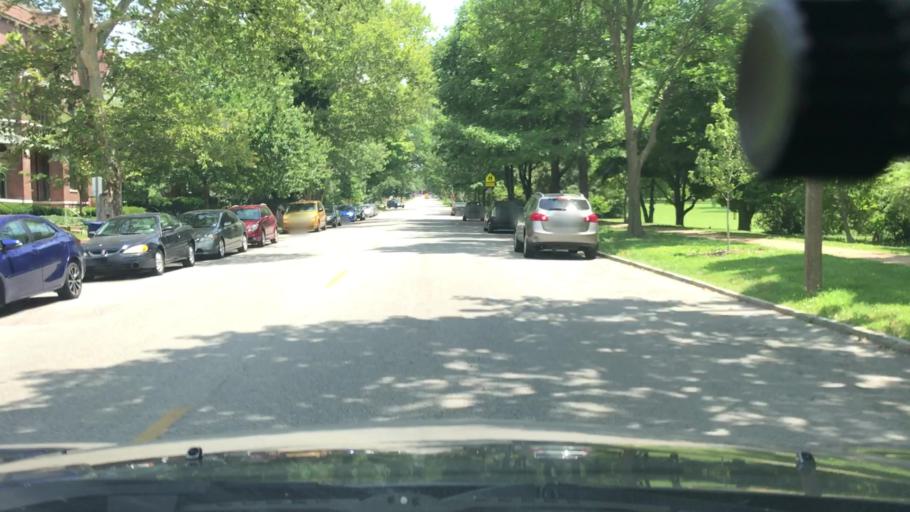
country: US
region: Missouri
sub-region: City of Saint Louis
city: St. Louis
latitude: 38.6079
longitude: -90.2487
